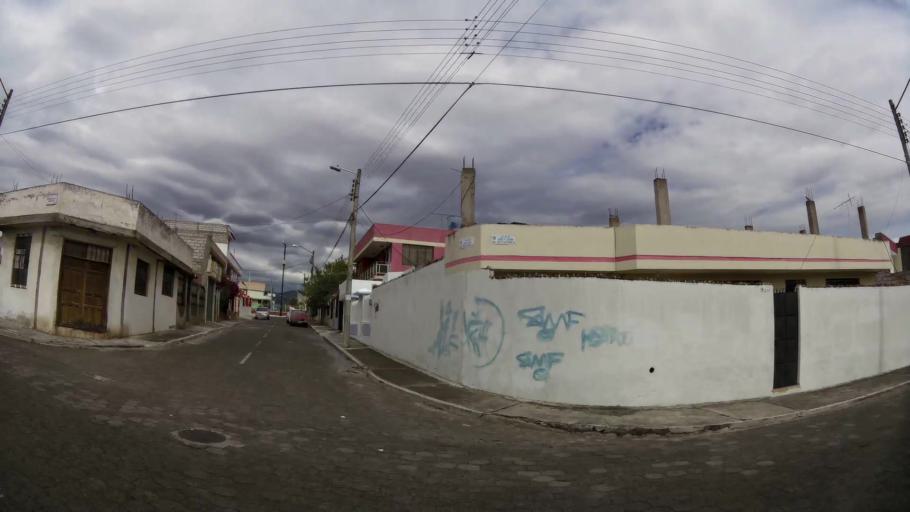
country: EC
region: Cotopaxi
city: Latacunga
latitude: -0.9246
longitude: -78.6235
